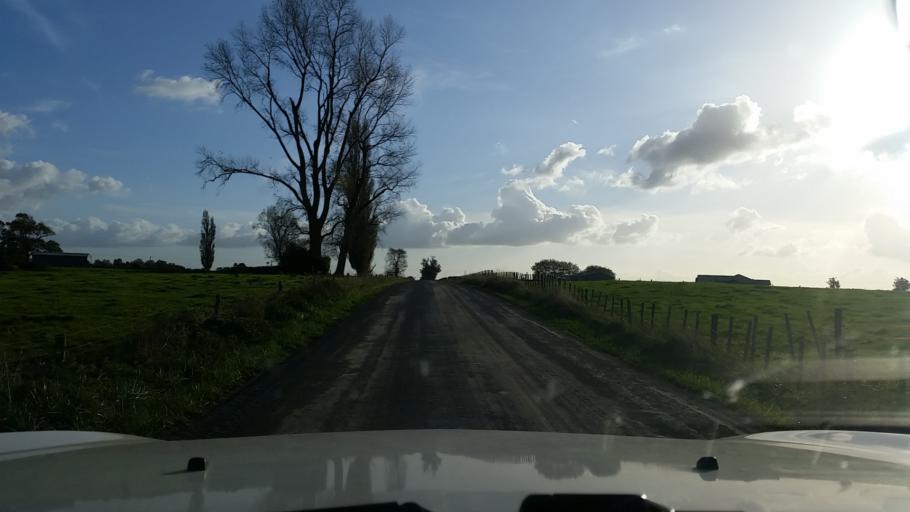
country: NZ
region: Bay of Plenty
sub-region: Western Bay of Plenty District
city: Katikati
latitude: -37.5775
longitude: 175.7286
